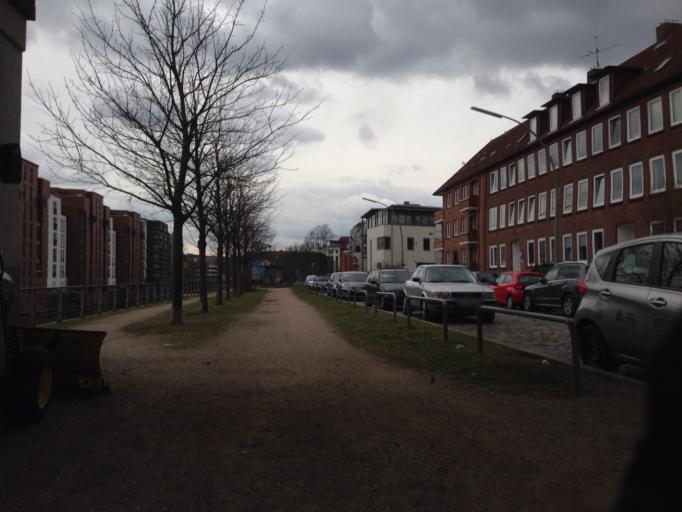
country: DE
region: Hamburg
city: Barmbek-Nord
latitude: 53.5841
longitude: 10.0462
